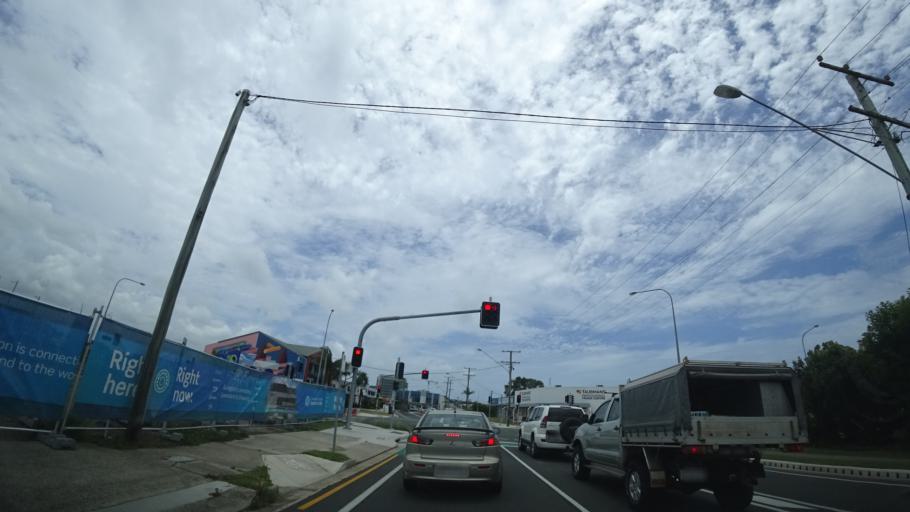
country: AU
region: Queensland
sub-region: Sunshine Coast
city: Mooloolaba
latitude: -26.6598
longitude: 153.0932
